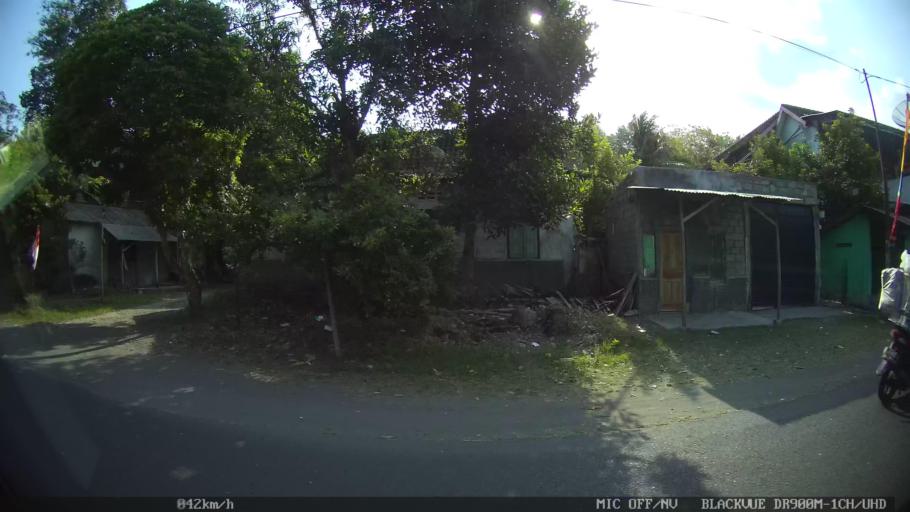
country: ID
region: Daerah Istimewa Yogyakarta
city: Bantul
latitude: -7.8712
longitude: 110.3166
